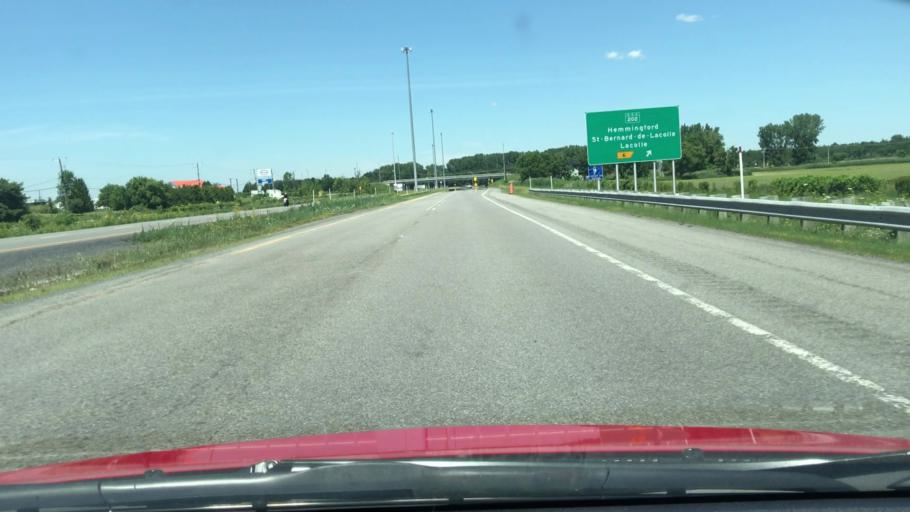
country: US
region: New York
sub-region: Clinton County
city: Champlain
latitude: 45.0632
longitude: -73.4542
